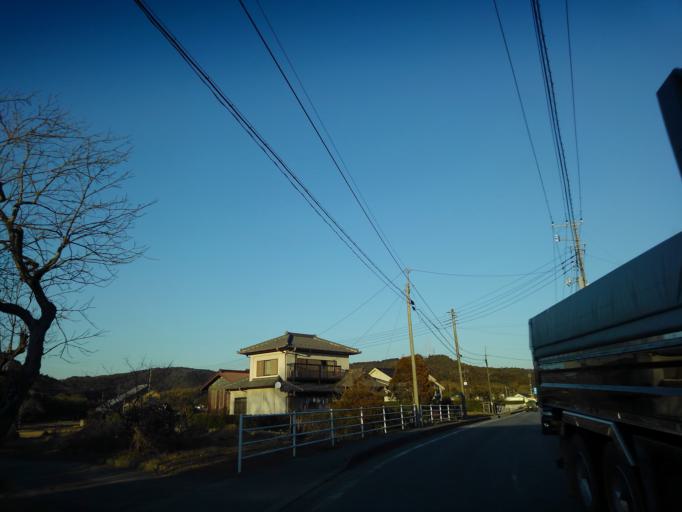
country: JP
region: Chiba
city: Kimitsu
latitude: 35.3011
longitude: 139.9834
